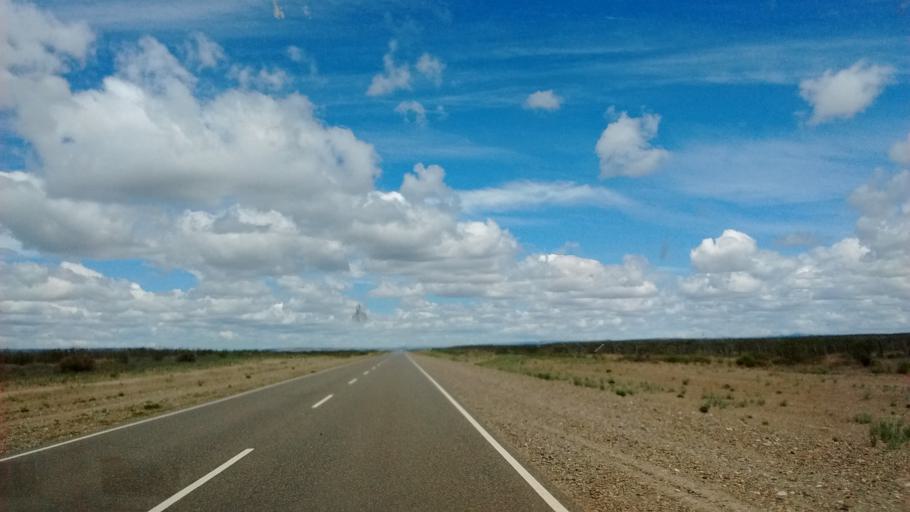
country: AR
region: Neuquen
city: Piedra del Aguila
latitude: -39.8273
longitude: -69.7494
